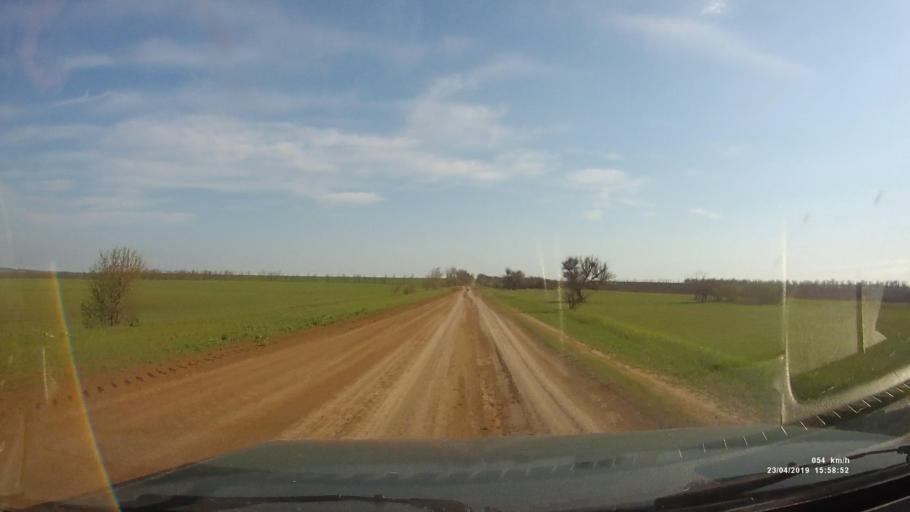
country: RU
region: Rostov
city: Remontnoye
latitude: 46.5206
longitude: 43.1095
